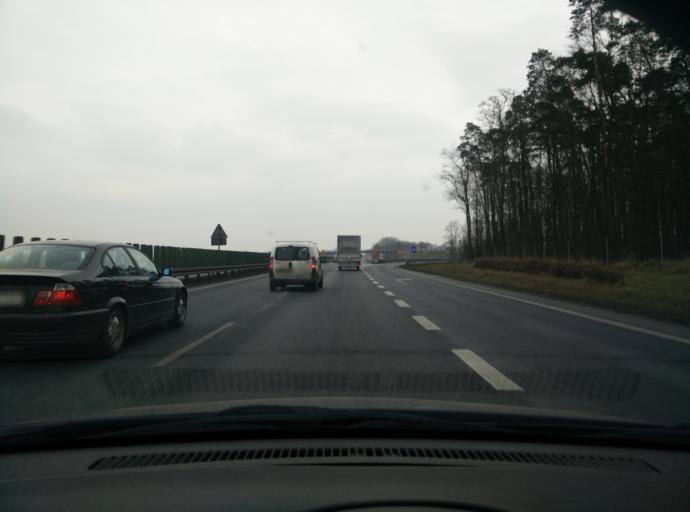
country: PL
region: Greater Poland Voivodeship
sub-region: Powiat poznanski
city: Daszewice
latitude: 52.3263
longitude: 17.0298
